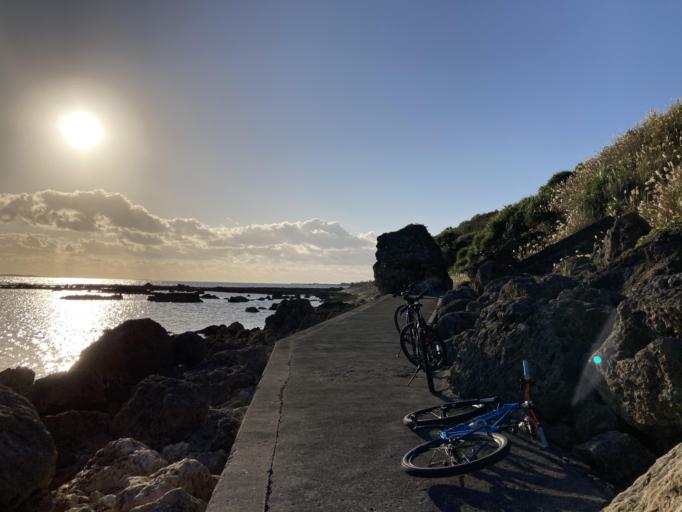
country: JP
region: Okinawa
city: Ginowan
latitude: 26.1898
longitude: 127.8217
